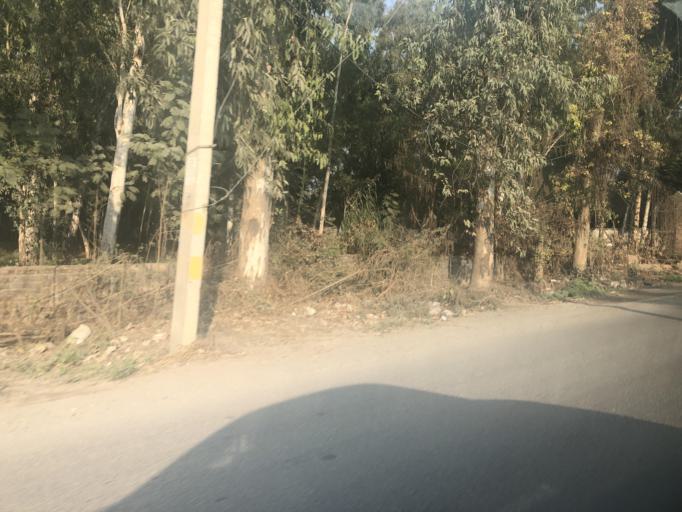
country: IN
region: Haryana
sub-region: Gurgaon
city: Gurgaon
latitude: 28.5423
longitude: 77.0175
